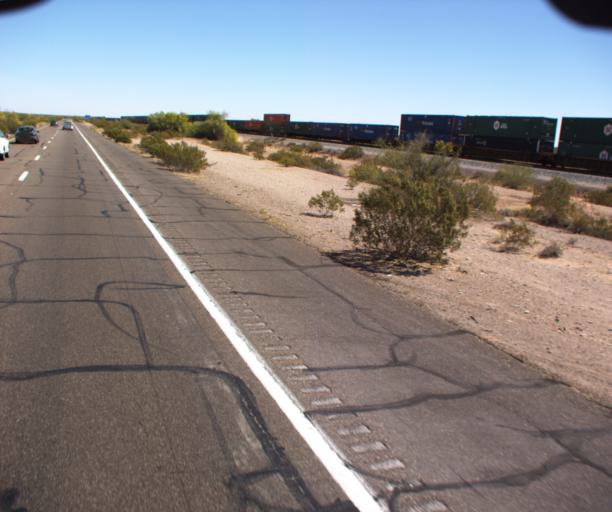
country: US
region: Arizona
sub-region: Maricopa County
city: Gila Bend
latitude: 32.8439
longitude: -113.2913
